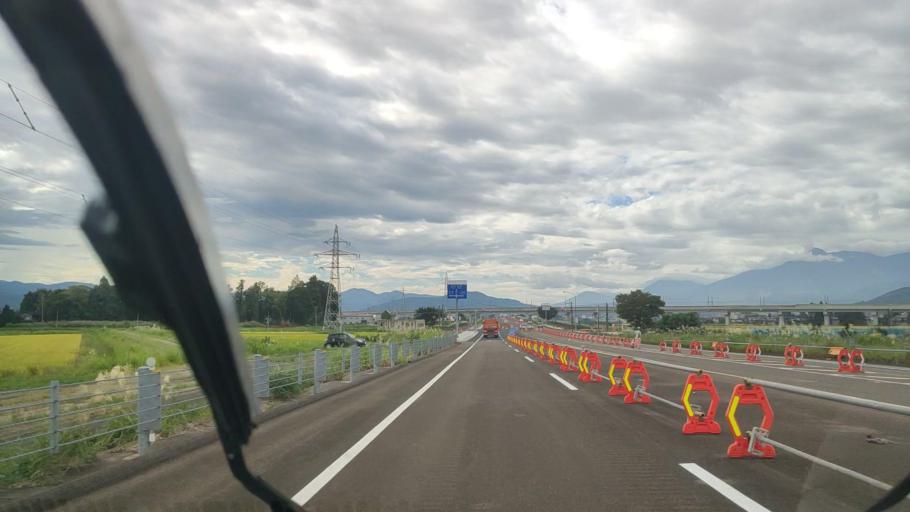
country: JP
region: Niigata
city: Joetsu
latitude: 37.0744
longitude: 138.2651
